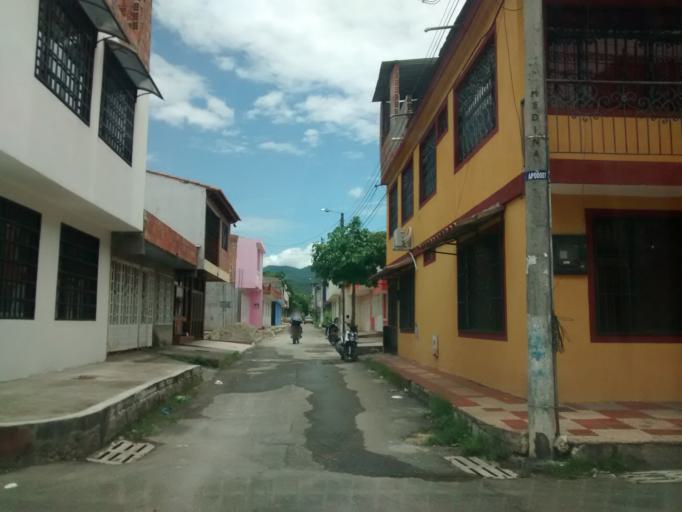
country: CO
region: Cundinamarca
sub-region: Girardot
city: Girardot City
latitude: 4.3103
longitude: -74.8061
